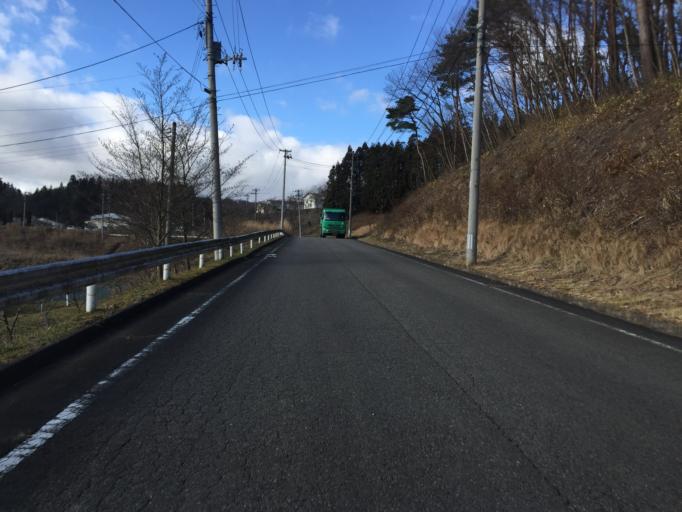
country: JP
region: Fukushima
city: Ishikawa
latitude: 37.2243
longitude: 140.5812
